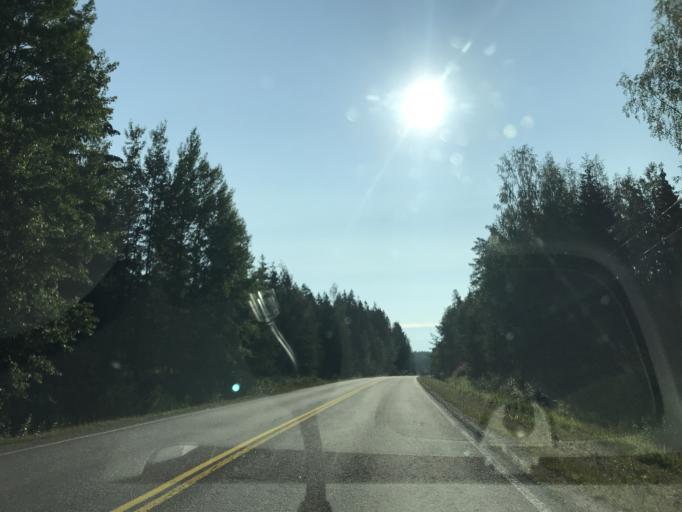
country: FI
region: Paijanne Tavastia
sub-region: Lahti
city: Orimattila
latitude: 60.7927
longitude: 25.6771
